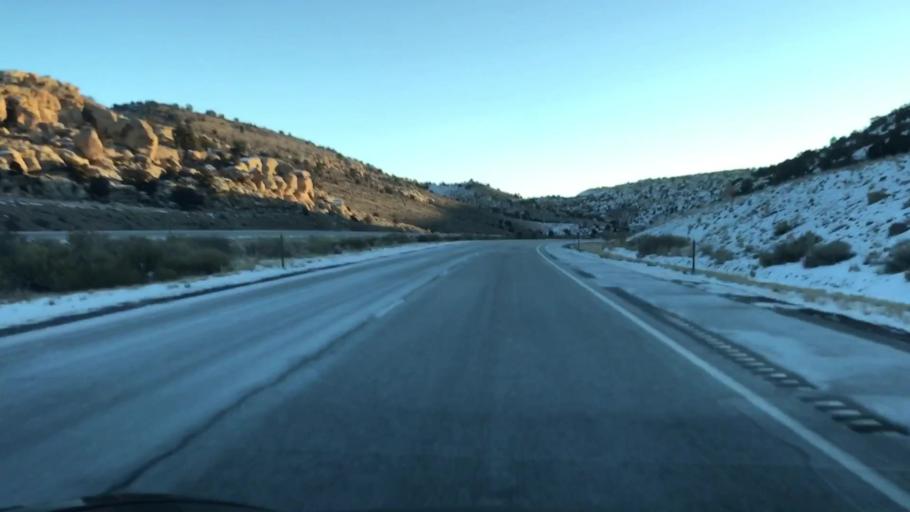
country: US
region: Utah
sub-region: Emery County
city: Ferron
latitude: 38.7989
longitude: -111.2773
